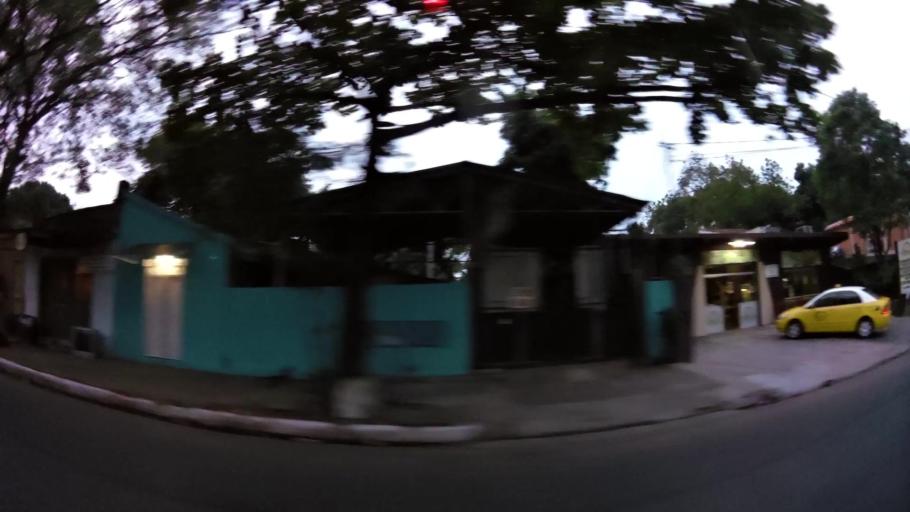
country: PY
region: Central
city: Lambare
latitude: -25.3312
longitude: -57.6025
